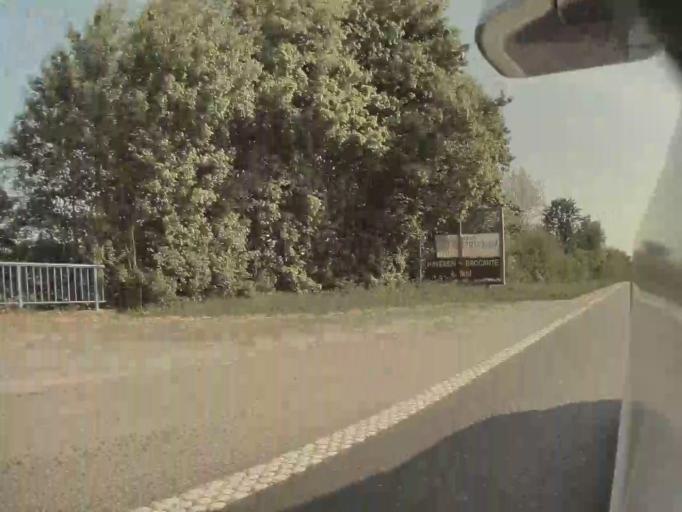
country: BE
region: Wallonia
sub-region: Province de Namur
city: Ciney
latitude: 50.3036
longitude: 5.1214
